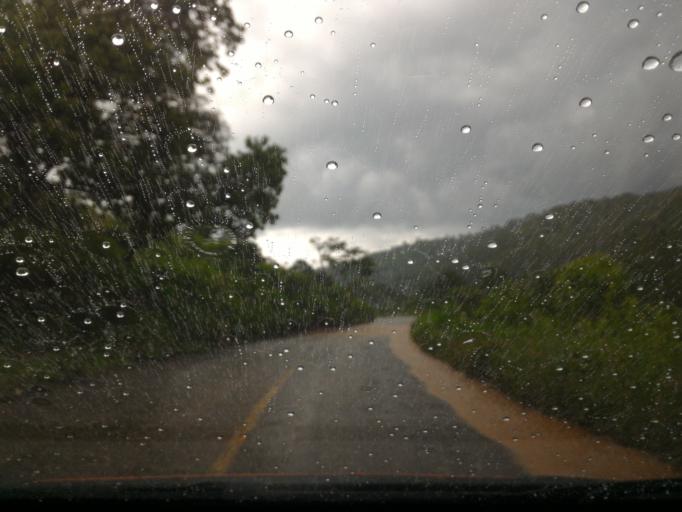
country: MX
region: Jalisco
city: San Andres Ixtlan
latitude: 19.8415
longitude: -103.4571
